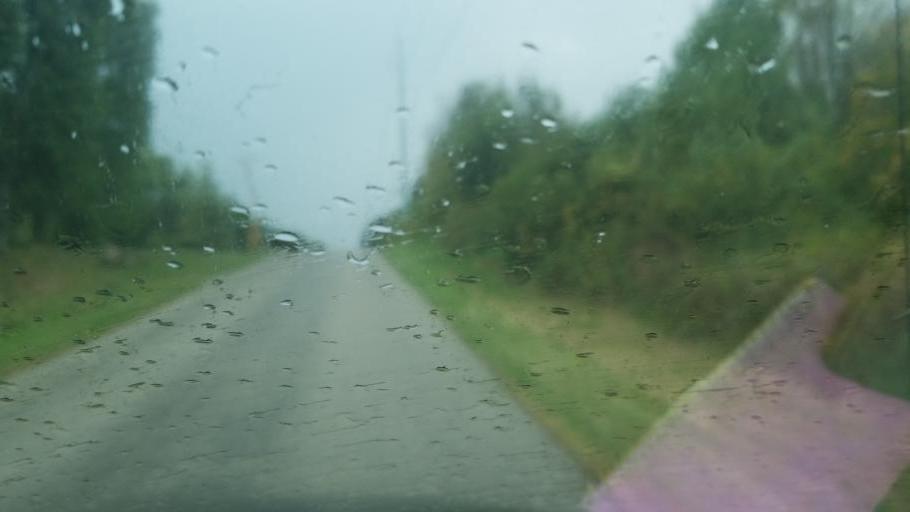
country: US
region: Ohio
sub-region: Sandusky County
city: Bellville
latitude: 40.5999
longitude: -82.5481
